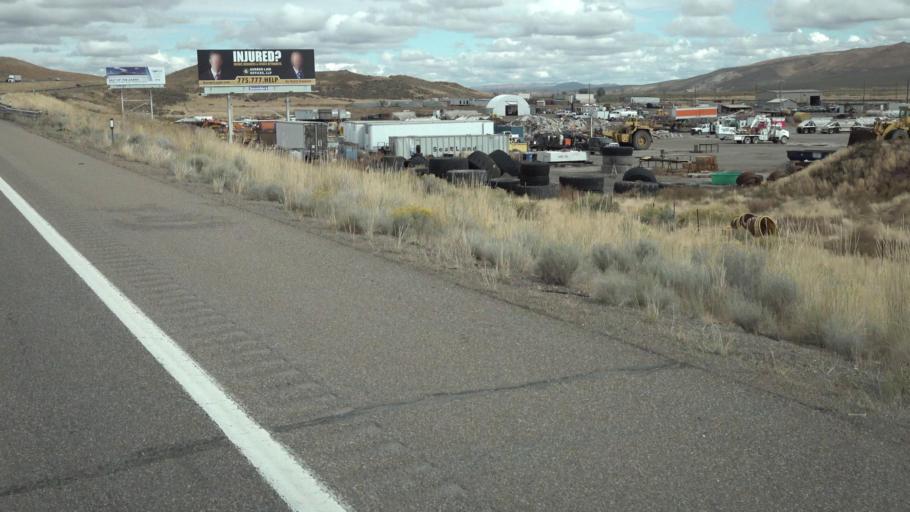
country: US
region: Nevada
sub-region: Elko County
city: Elko
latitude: 40.8890
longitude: -115.7132
